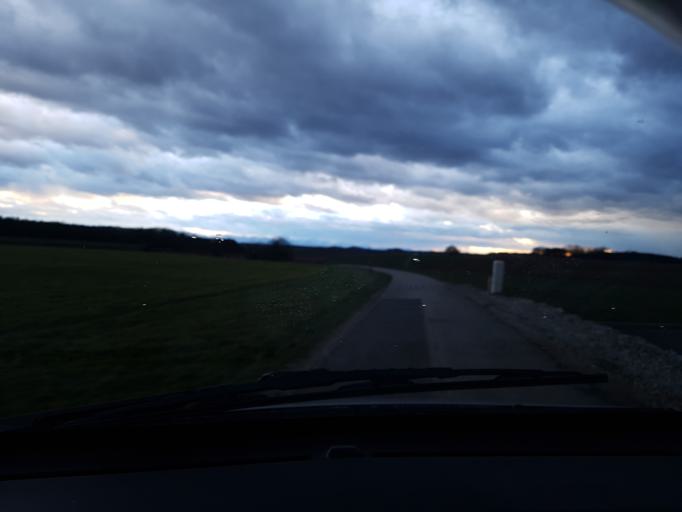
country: AT
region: Upper Austria
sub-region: Politischer Bezirk Linz-Land
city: Ansfelden
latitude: 48.1582
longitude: 14.3180
